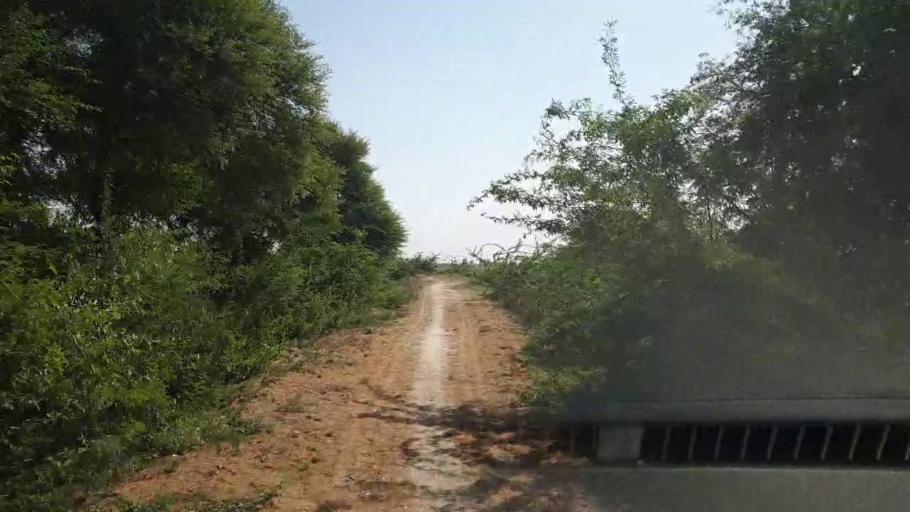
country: PK
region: Sindh
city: Kadhan
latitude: 24.6253
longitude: 68.9946
